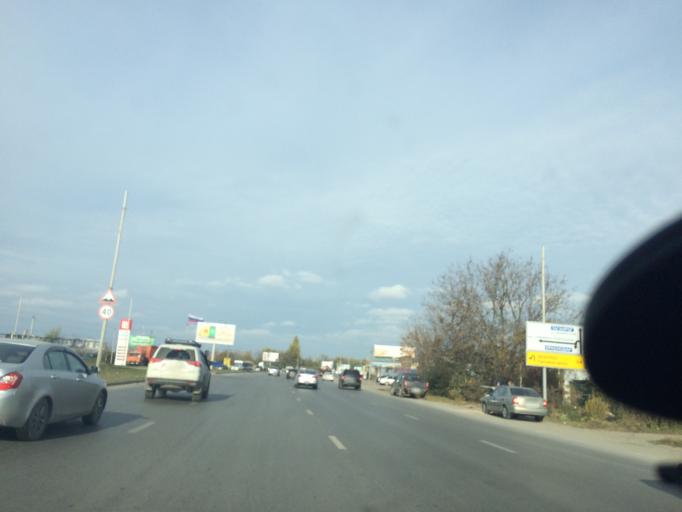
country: RU
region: Rostov
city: Severnyy
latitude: 47.2540
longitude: 39.6149
